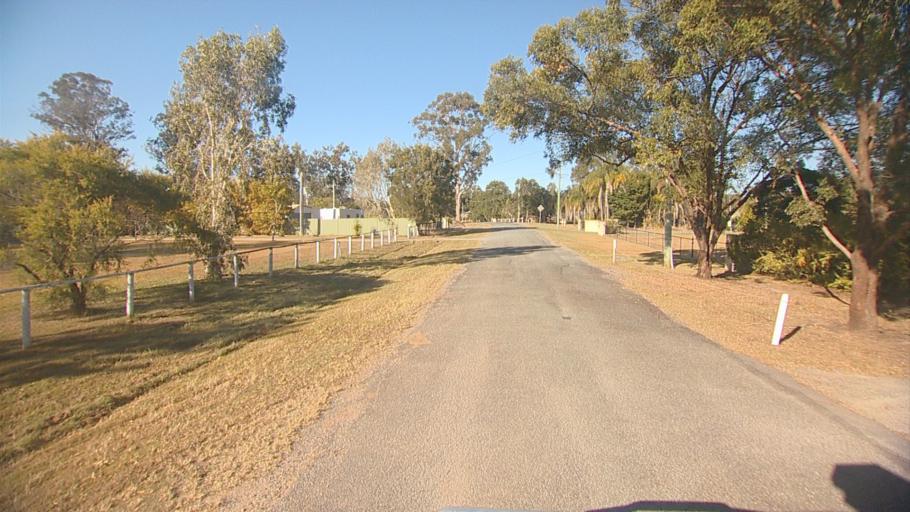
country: AU
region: Queensland
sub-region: Logan
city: Chambers Flat
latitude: -27.7601
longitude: 153.1047
